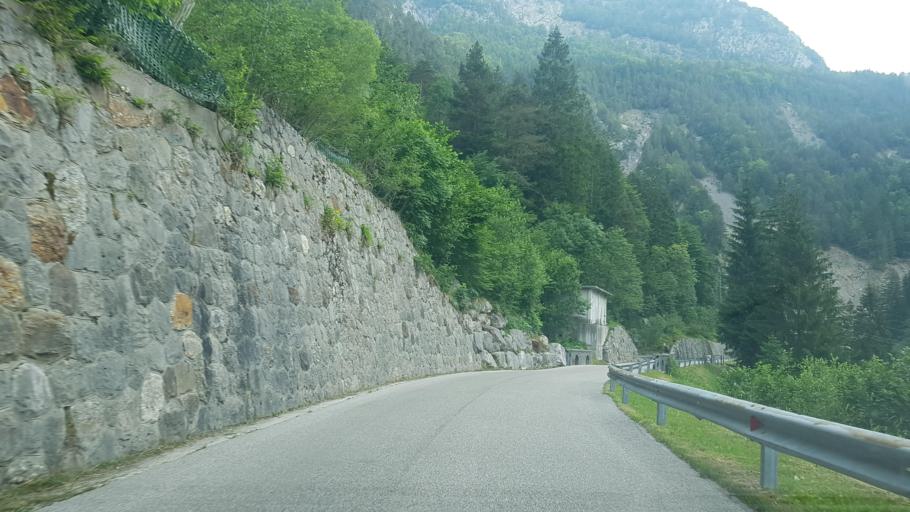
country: IT
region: Friuli Venezia Giulia
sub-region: Provincia di Udine
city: Pontebba
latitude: 46.5259
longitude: 13.2987
